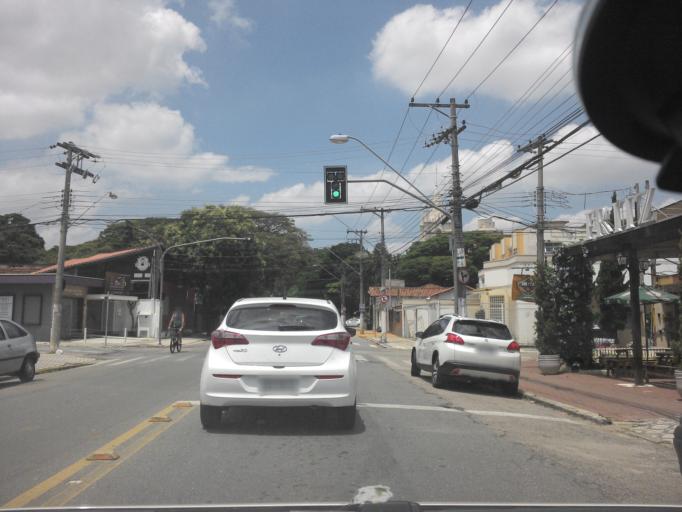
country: BR
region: Sao Paulo
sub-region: Taubate
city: Taubate
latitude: -23.0325
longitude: -45.5623
